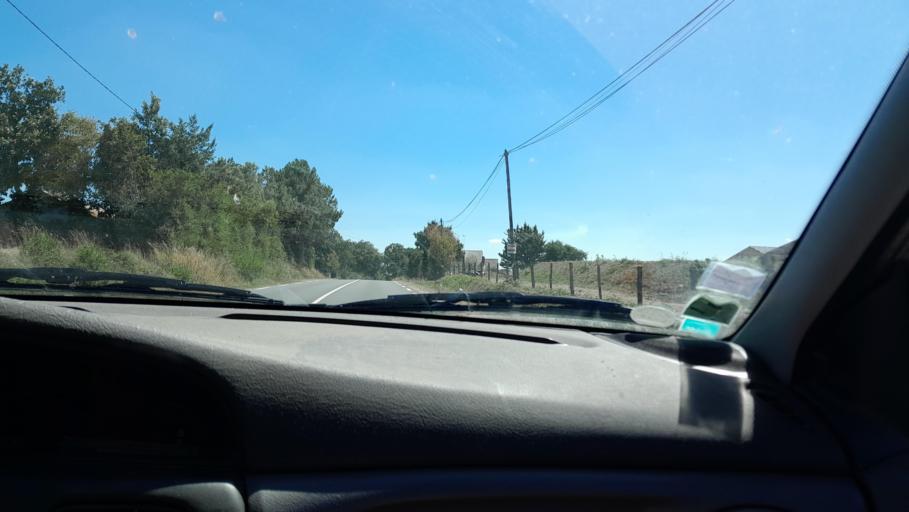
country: FR
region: Pays de la Loire
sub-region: Departement de la Loire-Atlantique
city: Saint-Mars-la-Jaille
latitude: 47.6167
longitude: -1.1982
